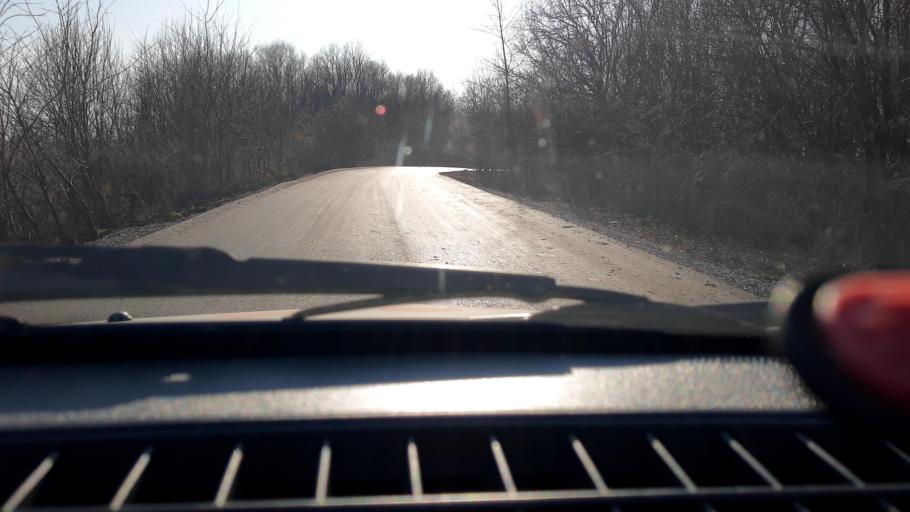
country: RU
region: Bashkortostan
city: Kabakovo
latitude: 54.6182
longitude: 56.1531
